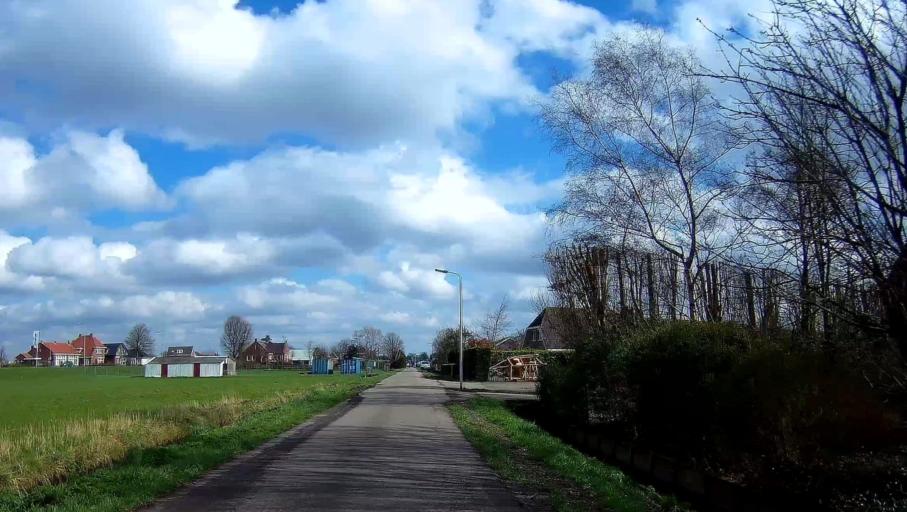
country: NL
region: South Holland
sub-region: Gemeente Zoetermeer
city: Zoetermeer
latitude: 52.0365
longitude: 4.4639
